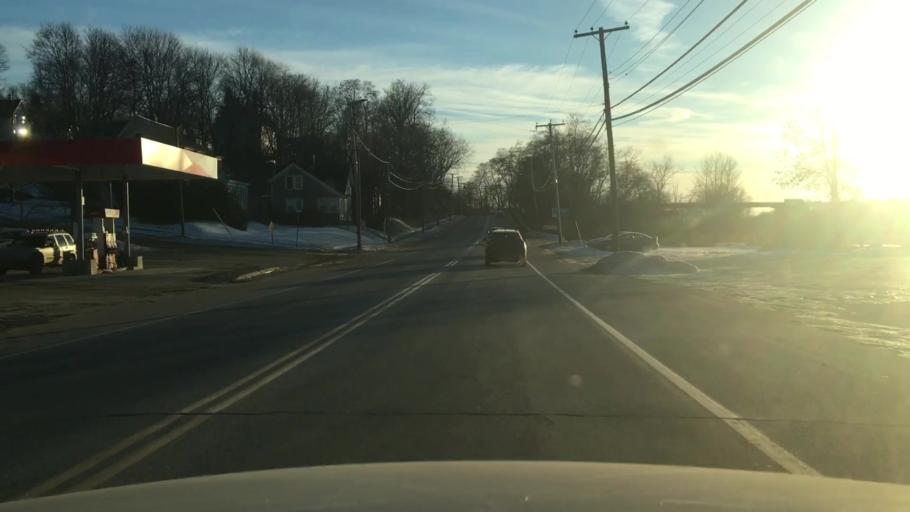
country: US
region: Maine
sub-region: Penobscot County
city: Brewer
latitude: 44.7905
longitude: -68.7691
